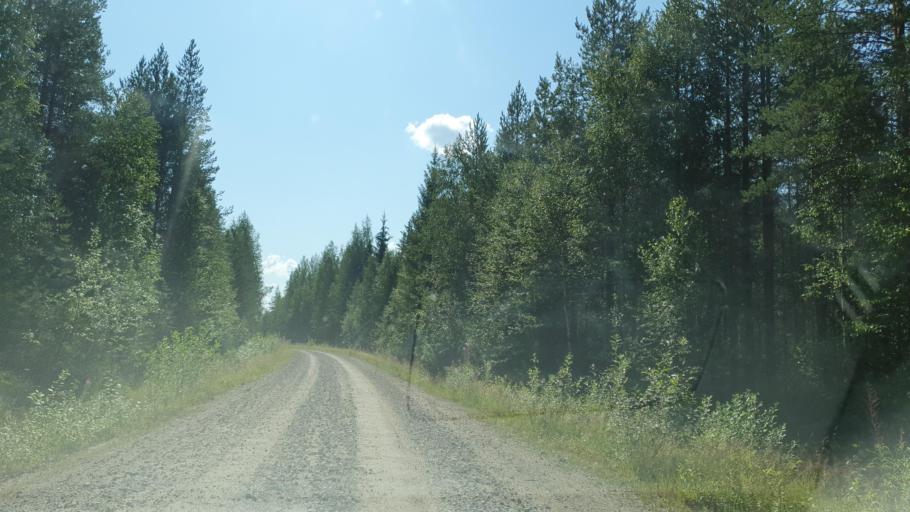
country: FI
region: Kainuu
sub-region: Kehys-Kainuu
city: Kuhmo
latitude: 64.0060
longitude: 29.5555
